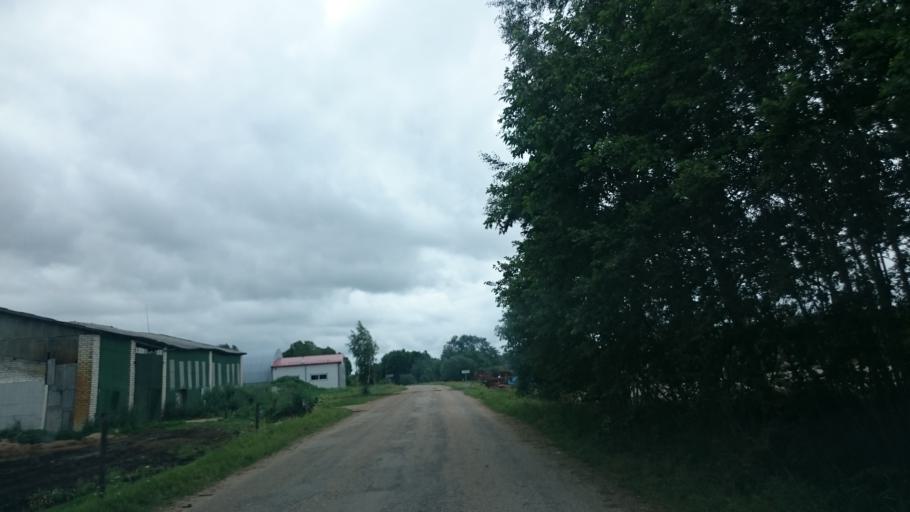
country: LV
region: Durbe
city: Liegi
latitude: 56.7469
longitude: 21.3675
